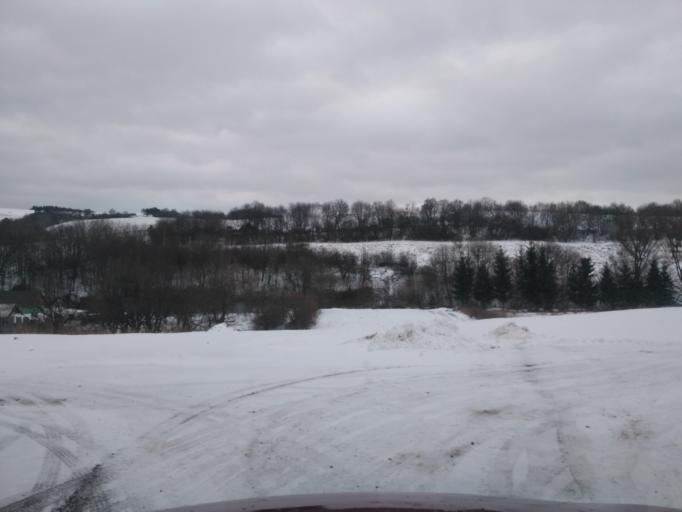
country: SK
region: Presovsky
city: Sabinov
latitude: 49.0560
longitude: 21.0607
